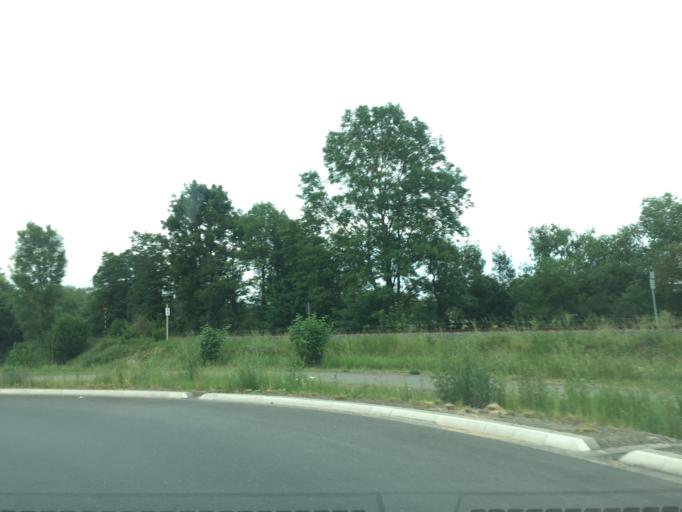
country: DE
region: Hesse
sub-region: Regierungsbezirk Giessen
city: Elz
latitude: 50.4294
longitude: 8.0346
